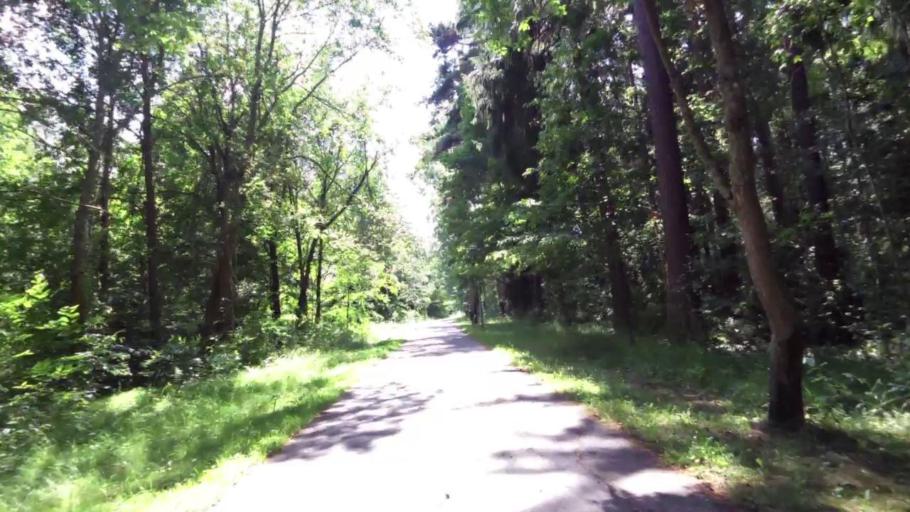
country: SE
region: OEstergoetland
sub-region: Linkopings Kommun
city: Linkoping
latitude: 58.4090
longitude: 15.5818
